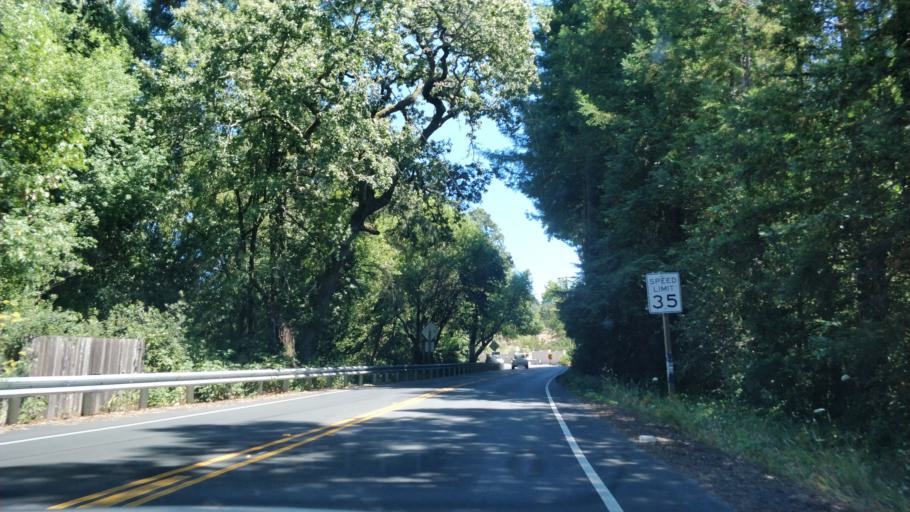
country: US
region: California
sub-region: Sonoma County
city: Graton
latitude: 38.3958
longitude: -122.8668
